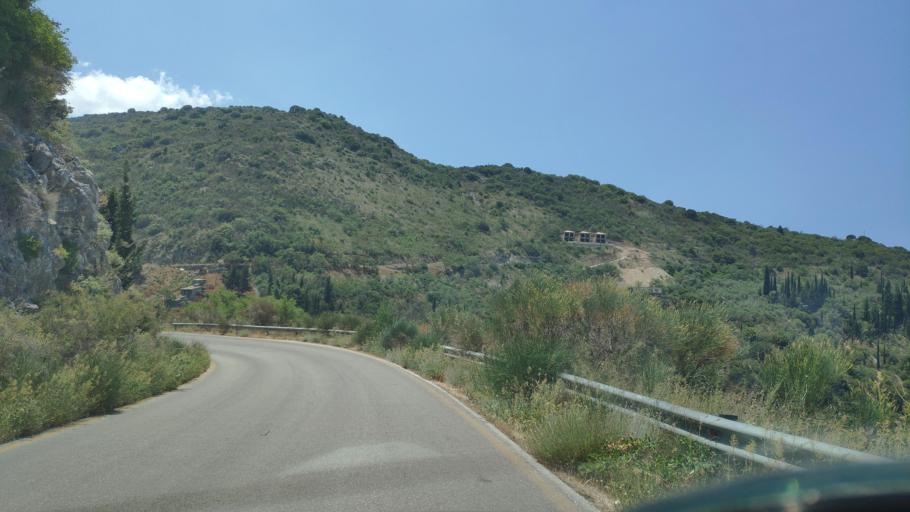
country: GR
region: Ionian Islands
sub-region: Lefkada
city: Nidri
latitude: 38.7473
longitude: 20.6204
